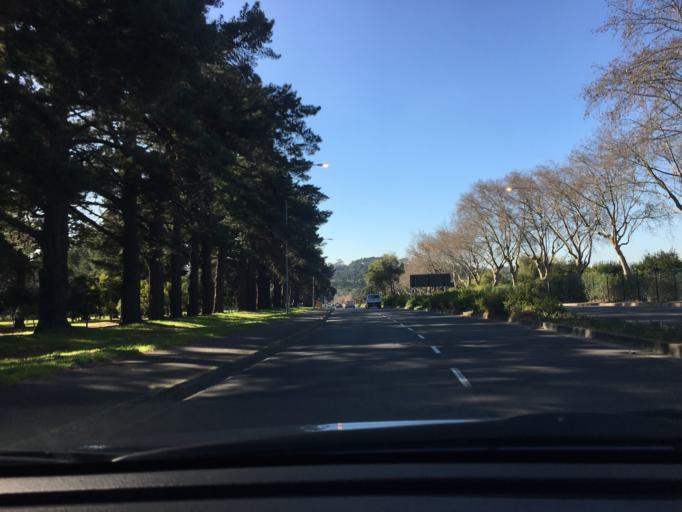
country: ZA
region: Western Cape
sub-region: City of Cape Town
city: Bergvliet
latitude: -34.0189
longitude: 18.4482
